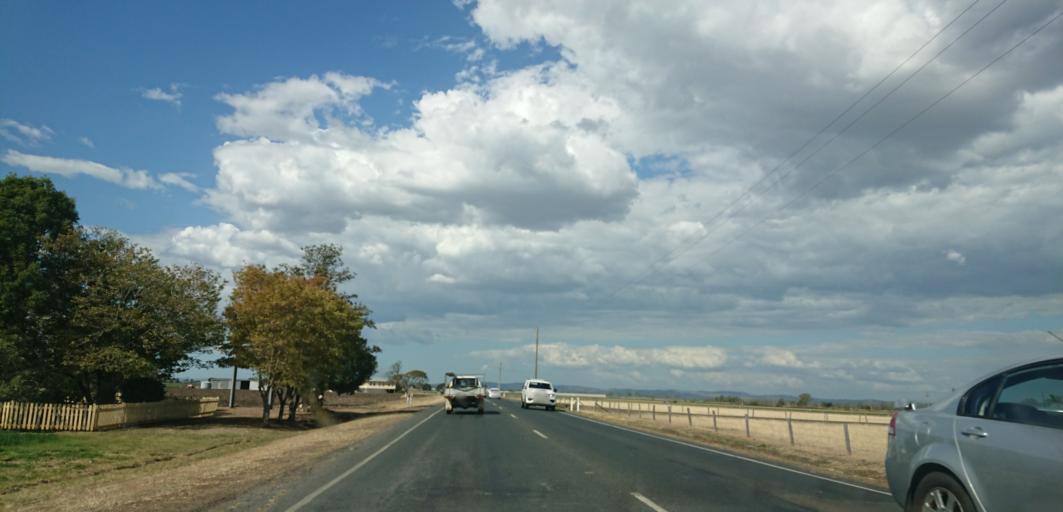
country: AU
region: Queensland
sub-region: Lockyer Valley
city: Gatton
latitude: -27.5545
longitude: 152.2945
